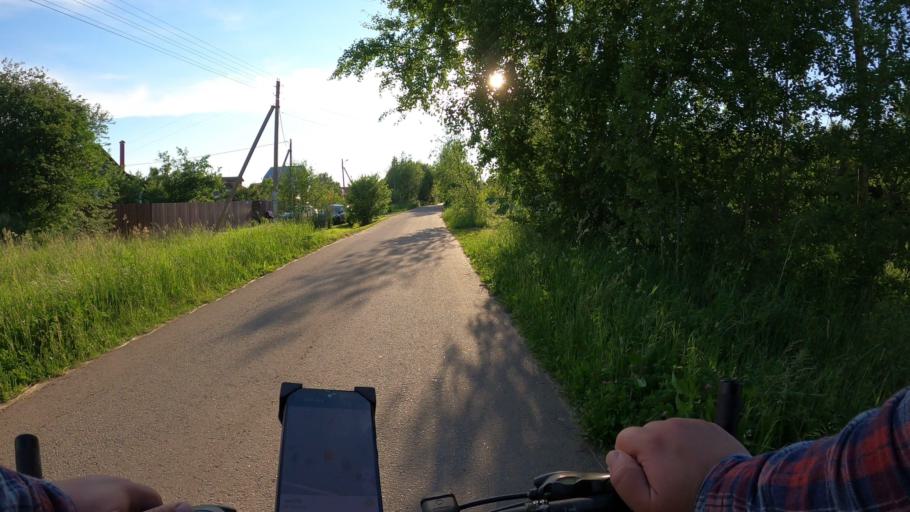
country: RU
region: Moskovskaya
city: Ashitkovo
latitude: 55.4568
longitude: 38.5769
